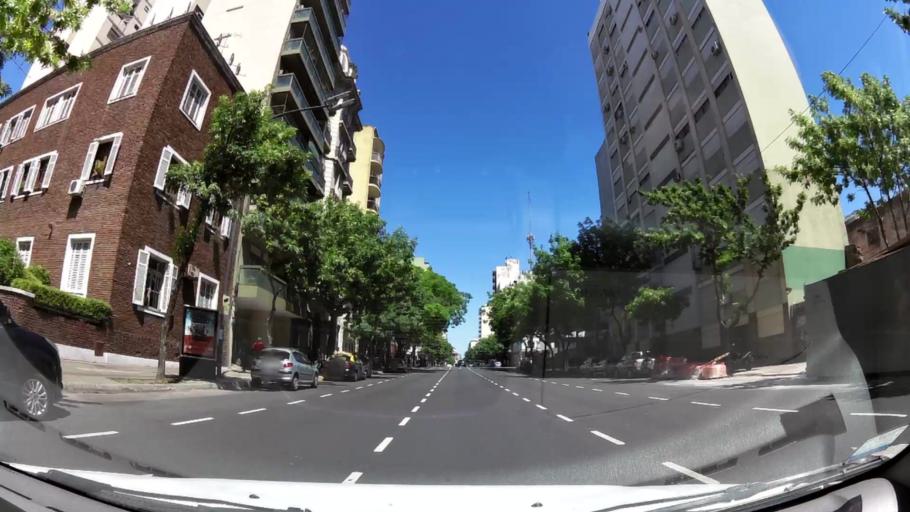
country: AR
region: Buenos Aires F.D.
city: Buenos Aires
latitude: -34.6173
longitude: -58.3735
